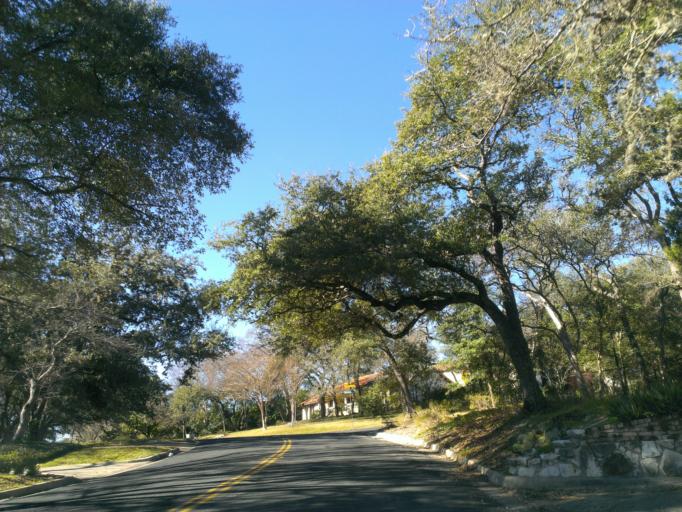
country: US
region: Texas
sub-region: Travis County
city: West Lake Hills
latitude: 30.3249
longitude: -97.7683
